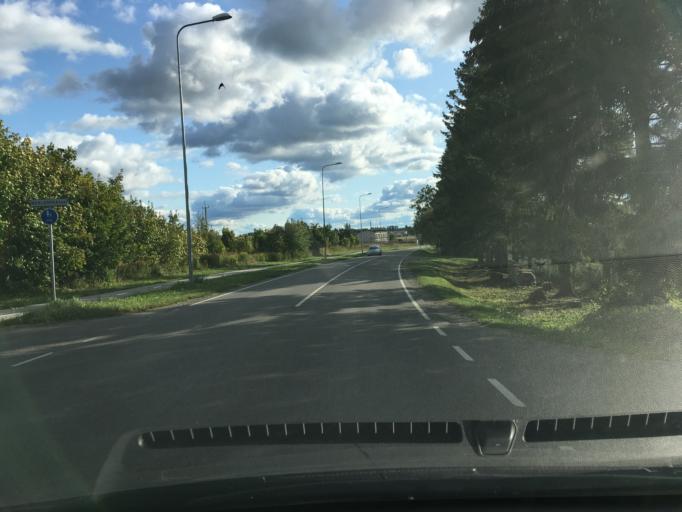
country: EE
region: Harju
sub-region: Joelaehtme vald
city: Loo
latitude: 59.4117
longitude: 24.9478
